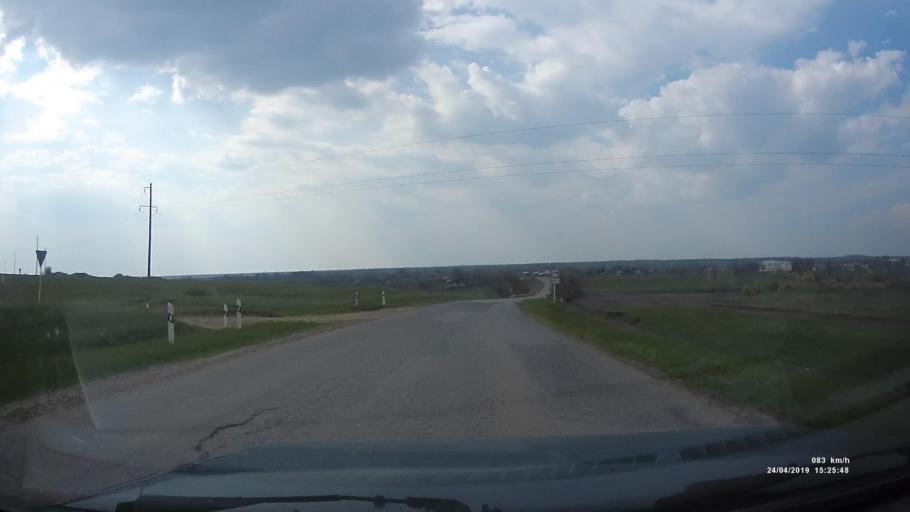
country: RU
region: Rostov
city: Remontnoye
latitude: 46.5542
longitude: 43.0407
